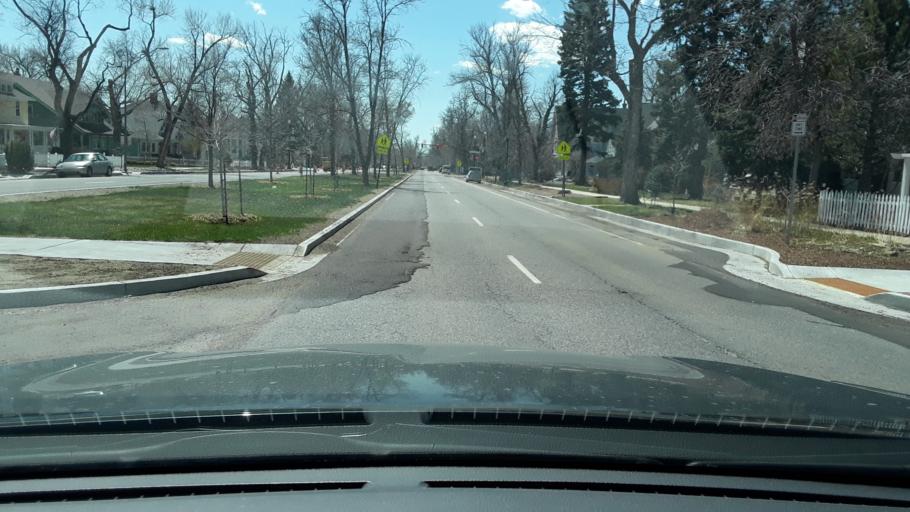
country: US
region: Colorado
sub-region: El Paso County
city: Colorado Springs
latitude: 38.8591
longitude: -104.8205
